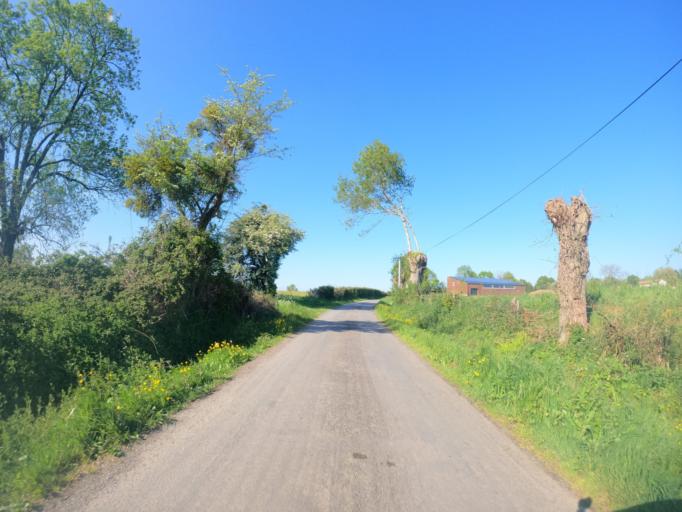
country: FR
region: Poitou-Charentes
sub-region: Departement des Deux-Sevres
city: Moncoutant
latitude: 46.7276
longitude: -0.5754
